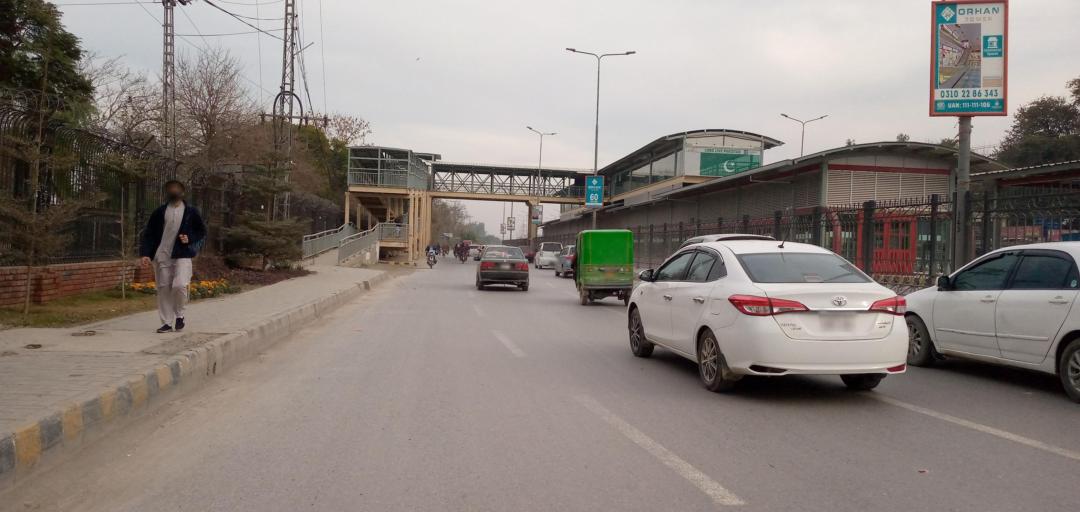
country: PK
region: Khyber Pakhtunkhwa
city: Peshawar
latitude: 33.9985
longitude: 71.4774
